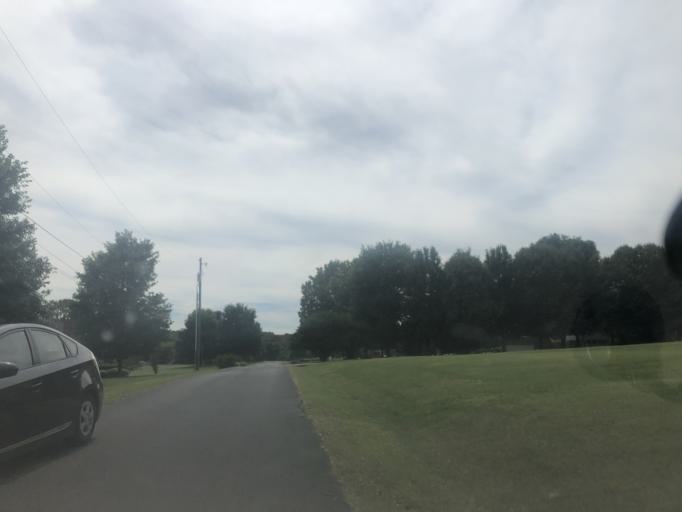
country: US
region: Tennessee
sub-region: Davidson County
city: Lakewood
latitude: 36.2272
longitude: -86.6708
